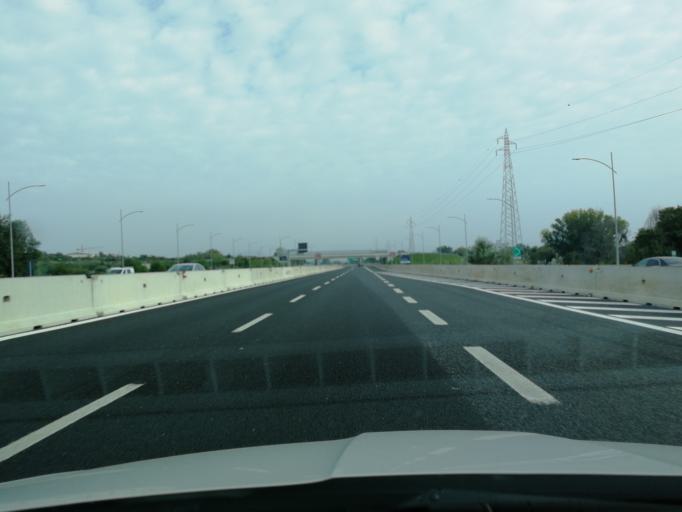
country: IT
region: Latium
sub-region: Citta metropolitana di Roma Capitale
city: Setteville
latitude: 41.9235
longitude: 12.6255
